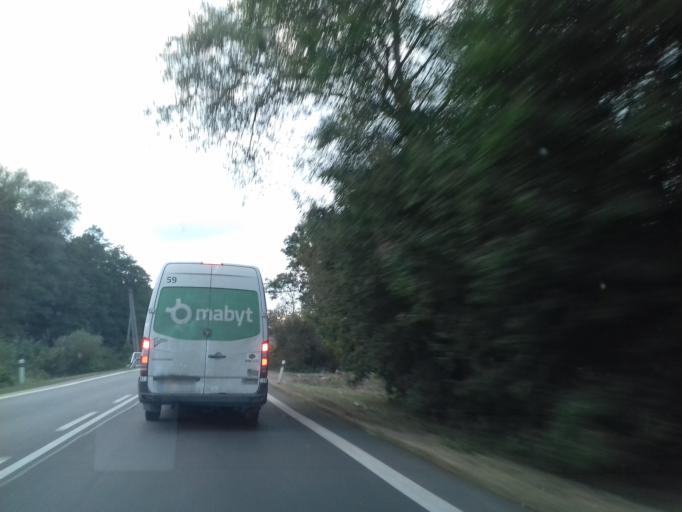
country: SK
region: Trenciansky
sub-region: Okres Trencin
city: Trencin
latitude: 48.9413
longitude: 17.9302
